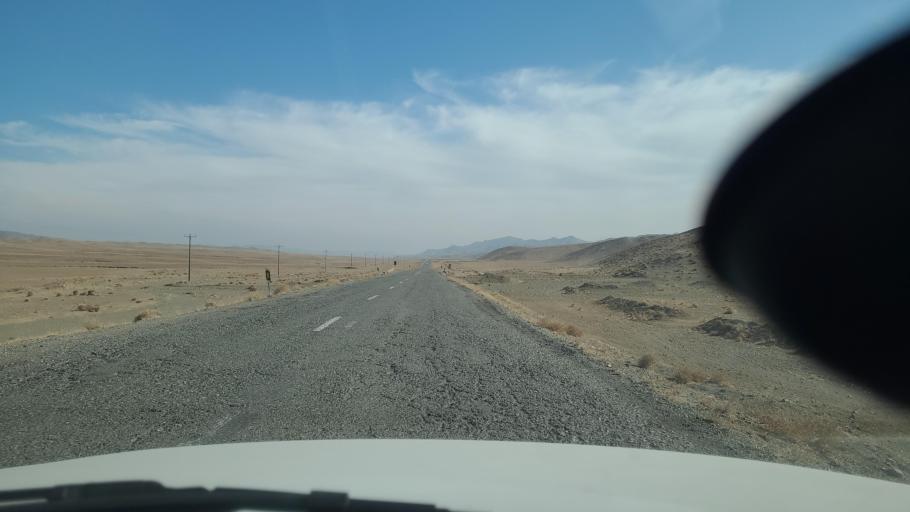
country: IR
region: Razavi Khorasan
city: Fariman
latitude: 35.5909
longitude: 59.6059
